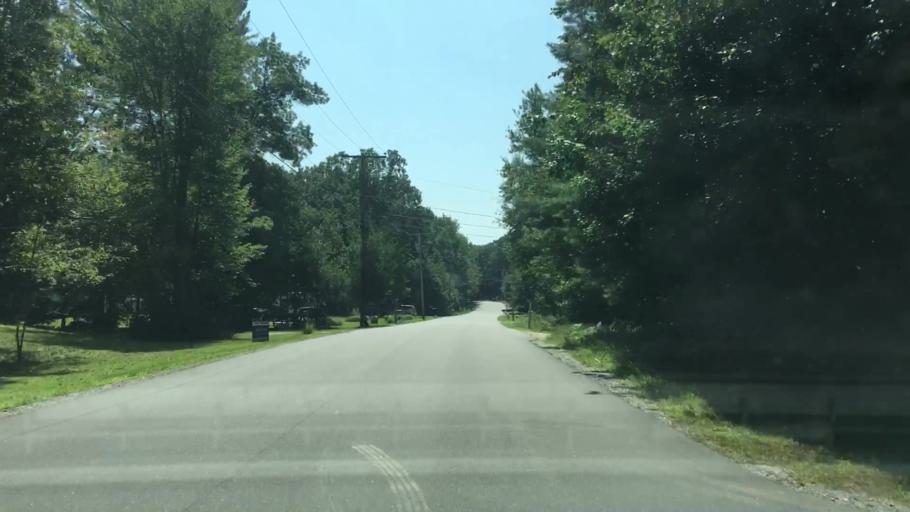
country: US
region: New Hampshire
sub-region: Rockingham County
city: Hampstead
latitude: 42.8917
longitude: -71.2174
